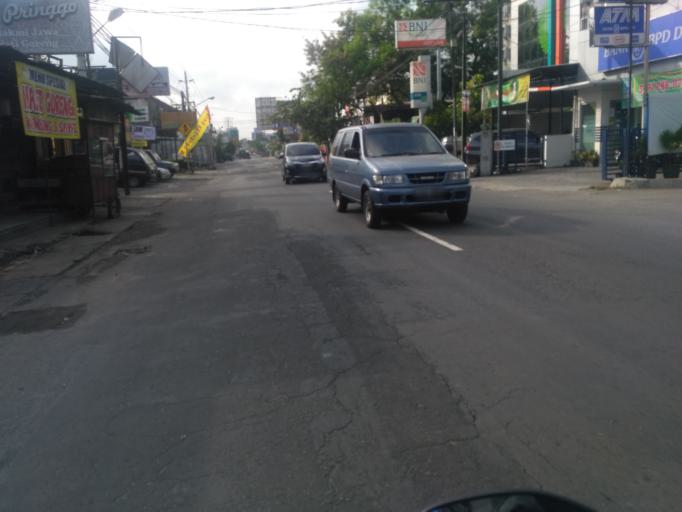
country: ID
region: Daerah Istimewa Yogyakarta
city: Gamping Lor
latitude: -7.7786
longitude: 110.3384
